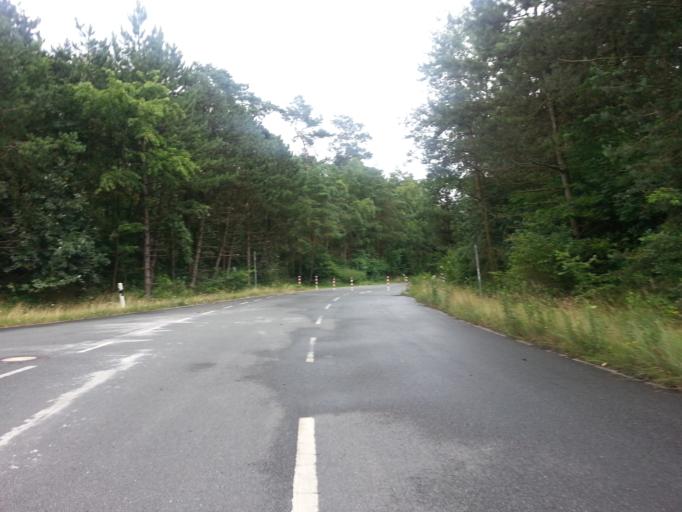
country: DE
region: North Rhine-Westphalia
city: Oer-Erkenschwick
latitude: 51.6975
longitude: 7.2581
